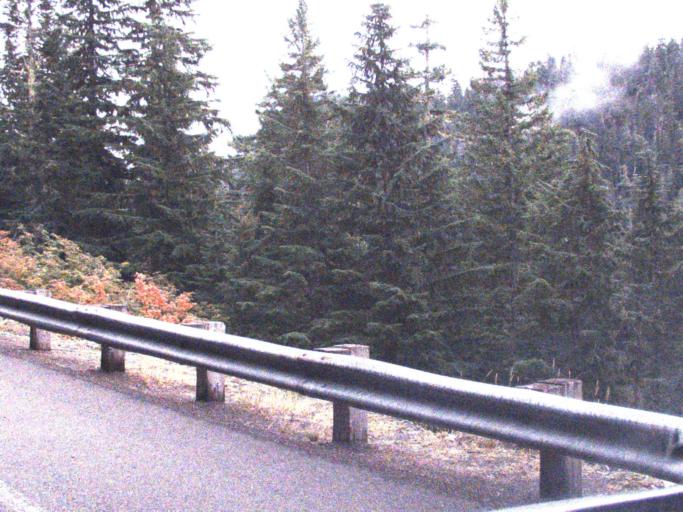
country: US
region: Washington
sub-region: Yakima County
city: Tieton
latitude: 46.6423
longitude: -121.4585
